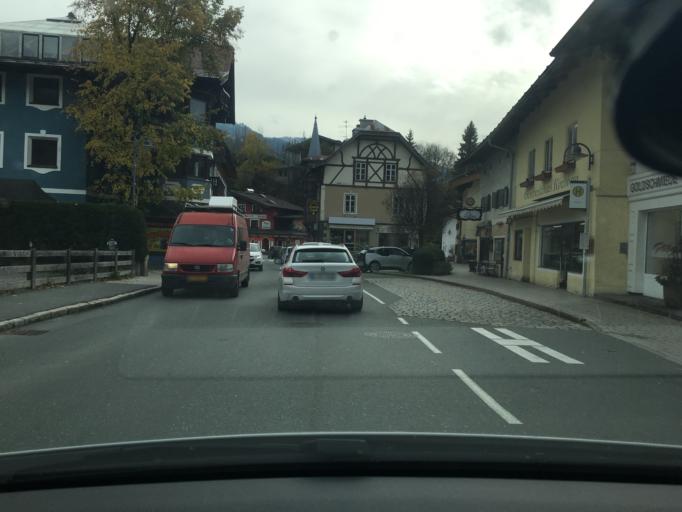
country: AT
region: Tyrol
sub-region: Politischer Bezirk Kitzbuhel
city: Kirchberg in Tirol
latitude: 47.4478
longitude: 12.3148
